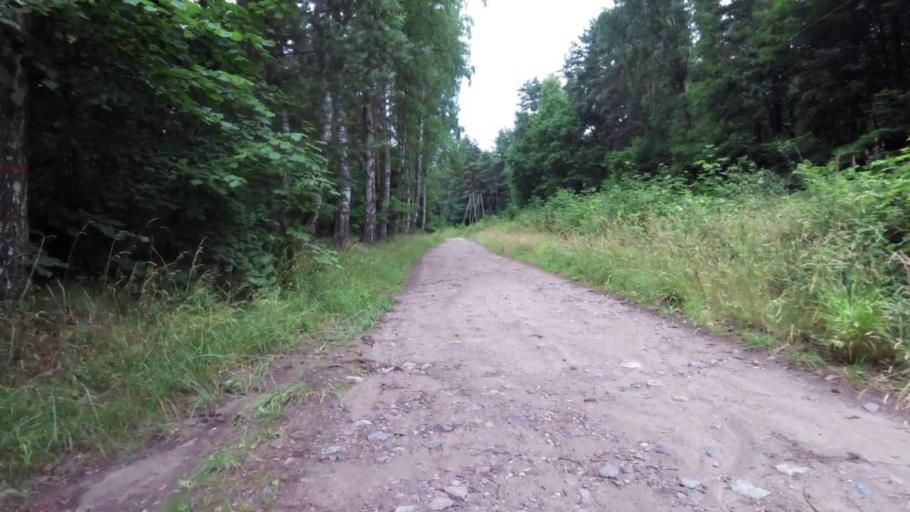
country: PL
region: West Pomeranian Voivodeship
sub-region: Powiat pyrzycki
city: Lipiany
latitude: 52.9747
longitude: 14.9268
